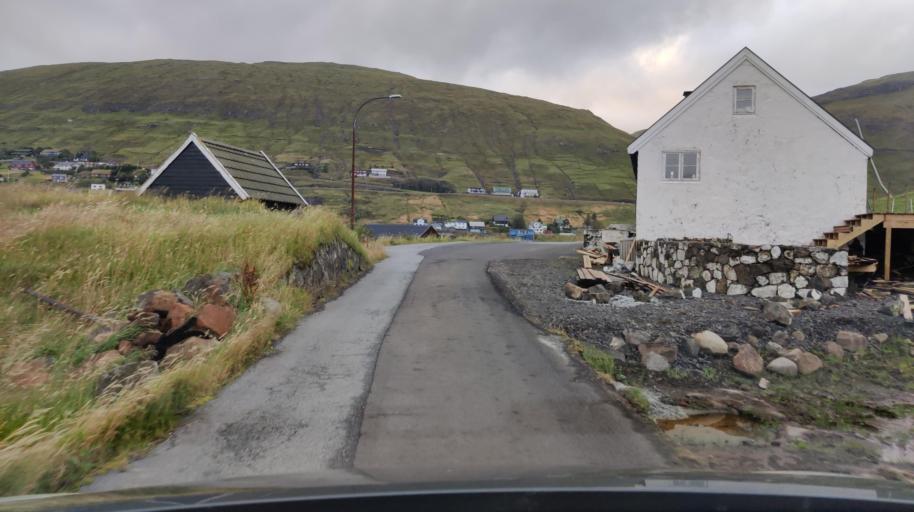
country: FO
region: Streymoy
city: Vestmanna
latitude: 62.1494
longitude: -7.1597
